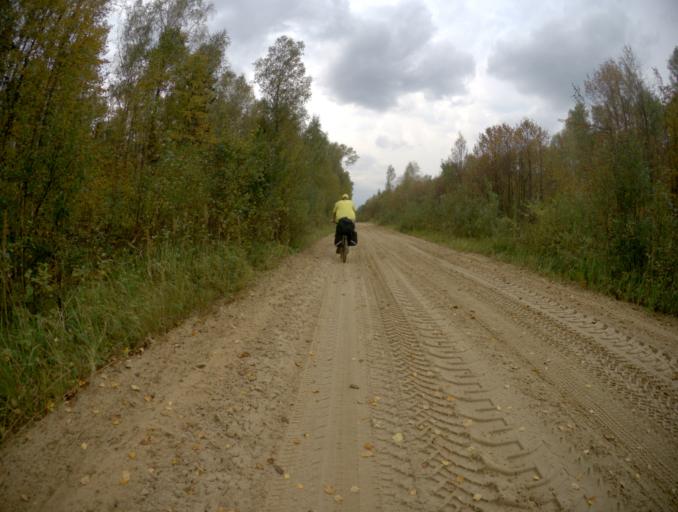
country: RU
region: Vladimir
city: Kideksha
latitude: 56.5003
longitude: 40.7742
